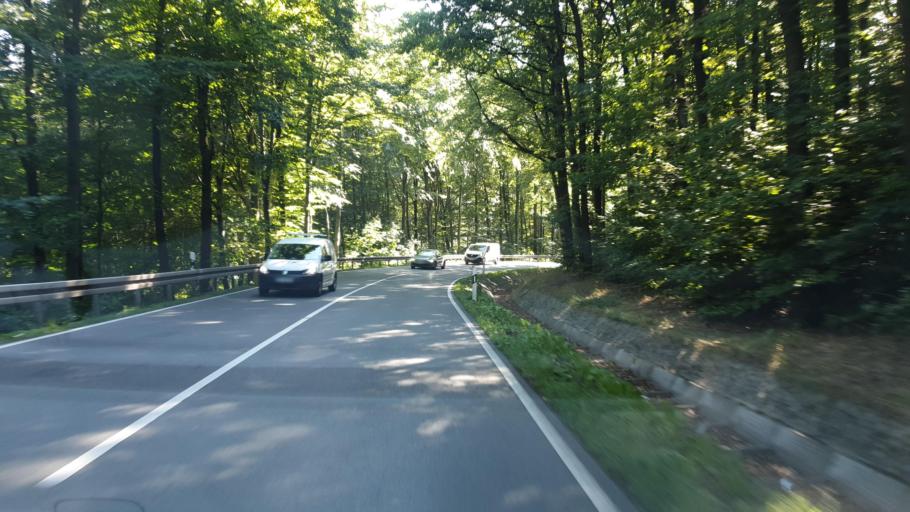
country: DE
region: Saxony
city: Lauter
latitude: 50.5870
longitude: 12.7406
